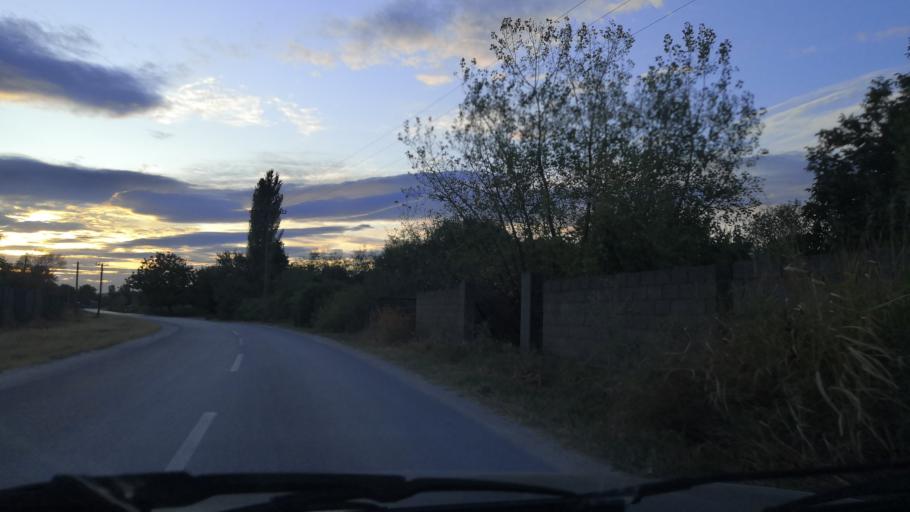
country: RO
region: Mehedinti
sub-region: Comuna Gogosu
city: Balta Verde
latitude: 44.2905
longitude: 22.6070
